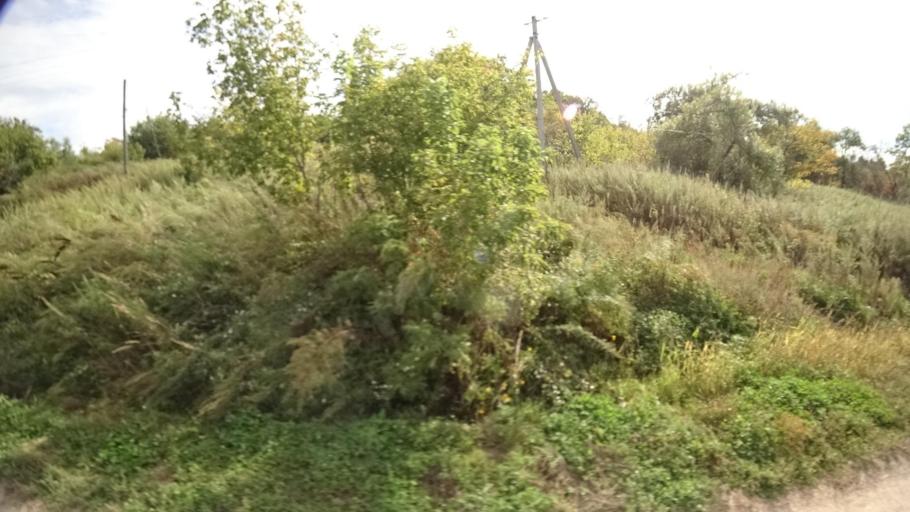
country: RU
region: Primorskiy
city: Dostoyevka
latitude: 44.3288
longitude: 133.4800
